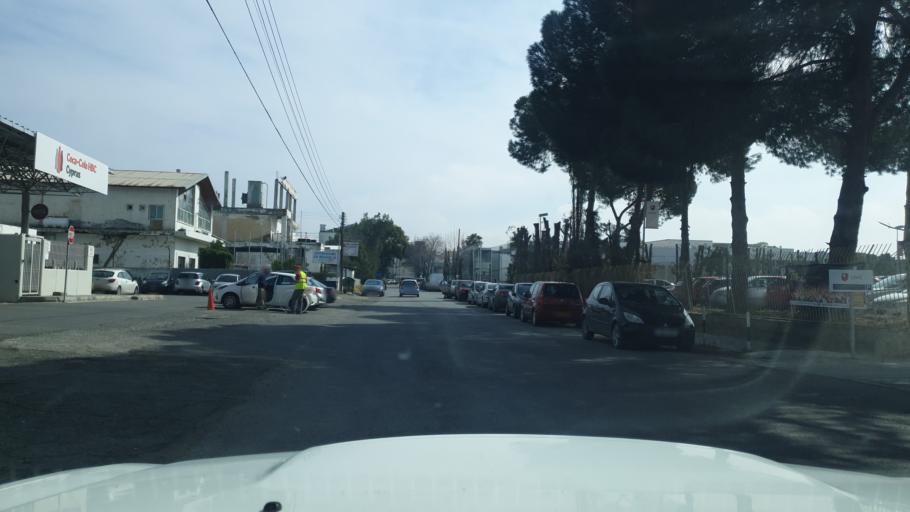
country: CY
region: Lefkosia
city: Nicosia
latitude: 35.1662
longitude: 33.3224
